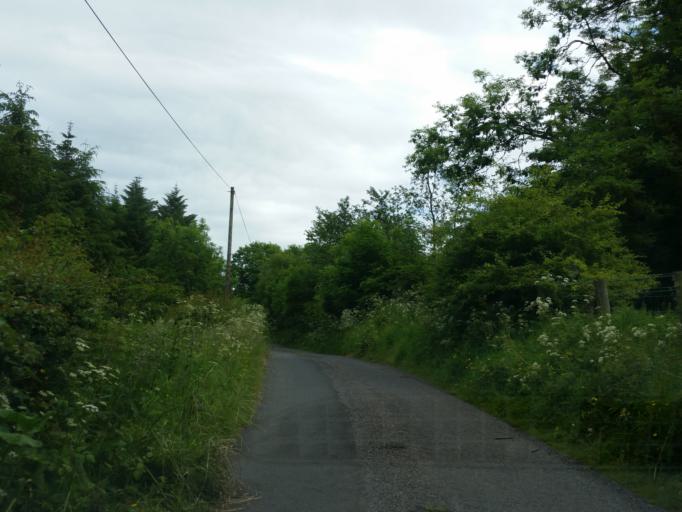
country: GB
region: Northern Ireland
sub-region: Omagh District
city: Omagh
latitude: 54.5584
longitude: -7.0778
